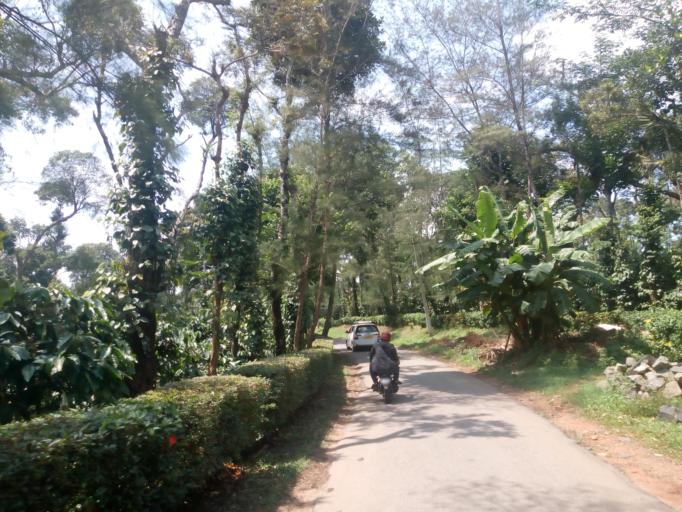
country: IN
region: Karnataka
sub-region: Kodagu
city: Ponnampet
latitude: 12.0322
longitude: 75.9504
